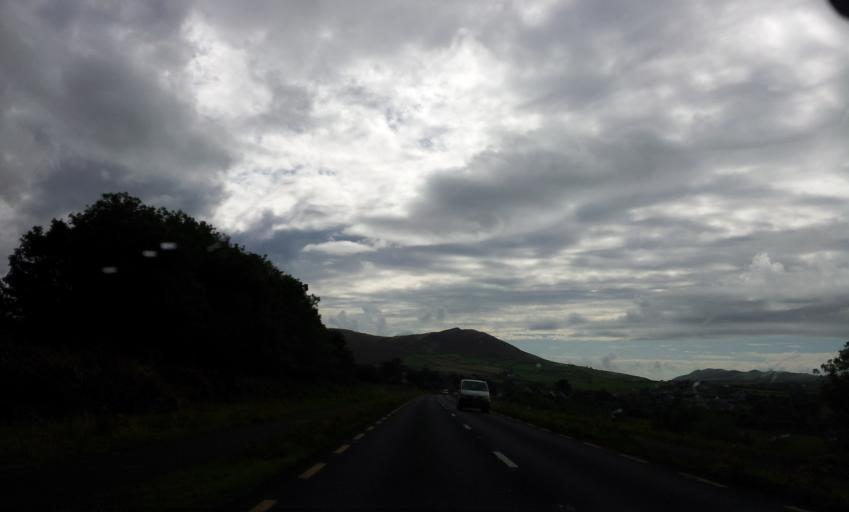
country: IE
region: Munster
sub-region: Ciarrai
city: Dingle
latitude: 52.1576
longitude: -10.0404
